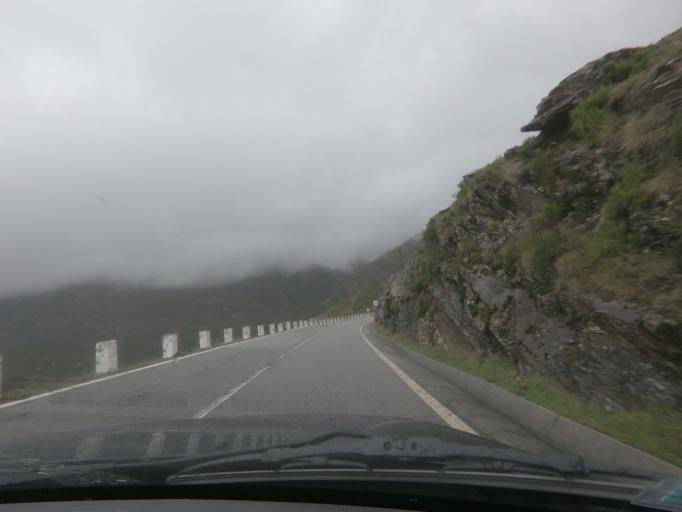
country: PT
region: Vila Real
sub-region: Mondim de Basto
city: Mondim de Basto
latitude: 41.3385
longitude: -7.8753
